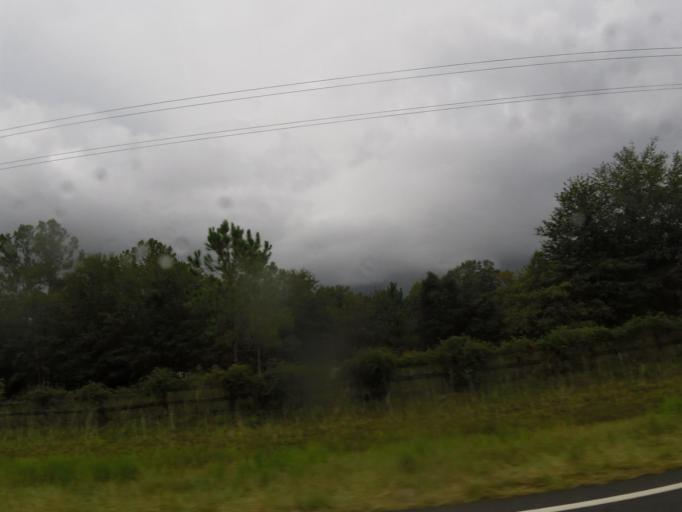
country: US
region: Florida
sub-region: Baker County
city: Macclenny
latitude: 30.3686
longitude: -82.1442
